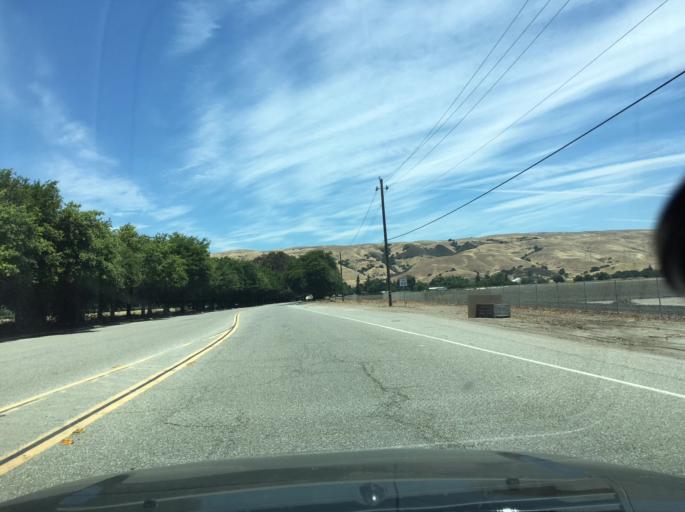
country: US
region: California
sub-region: Santa Clara County
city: Morgan Hill
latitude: 37.2014
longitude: -121.7360
